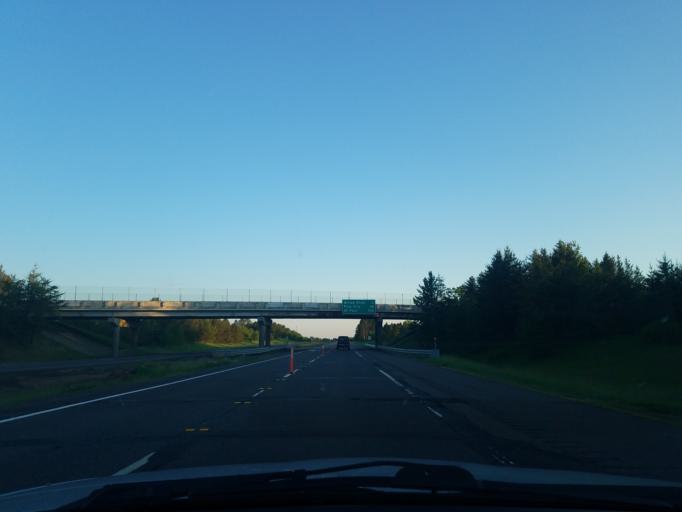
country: US
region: Minnesota
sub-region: Carlton County
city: Moose Lake
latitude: 46.3469
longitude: -92.8114
